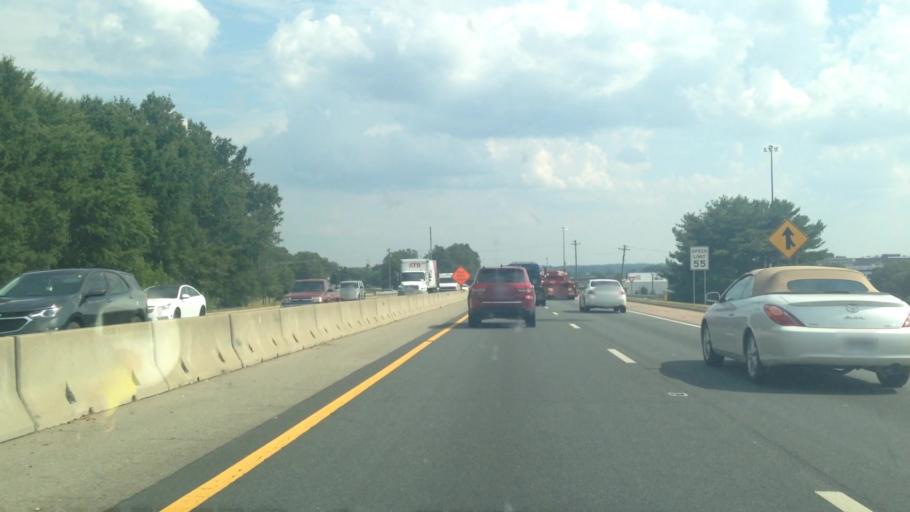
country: US
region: North Carolina
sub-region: Forsyth County
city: Winston-Salem
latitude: 36.1074
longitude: -80.2361
